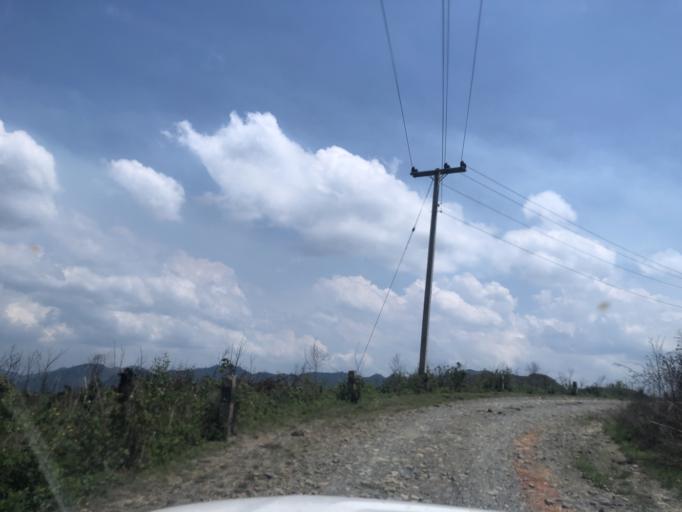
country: LA
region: Phongsali
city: Phongsali
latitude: 21.4200
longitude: 102.1849
